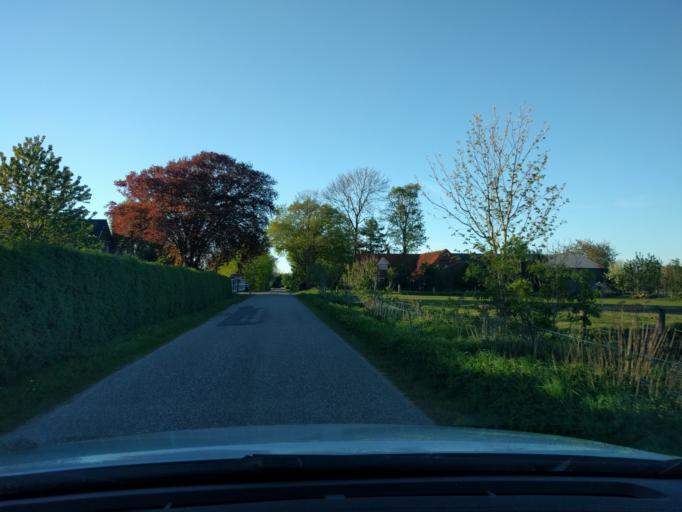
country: DK
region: South Denmark
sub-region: Nyborg Kommune
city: Ullerslev
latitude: 55.3957
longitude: 10.6488
